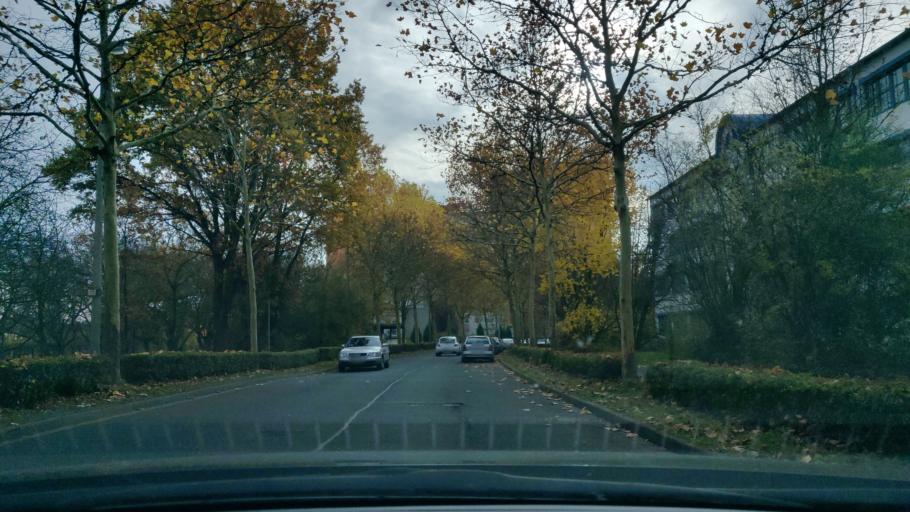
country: DE
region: Hesse
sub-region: Regierungsbezirk Kassel
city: Fuldabruck
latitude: 51.2826
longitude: 9.4502
